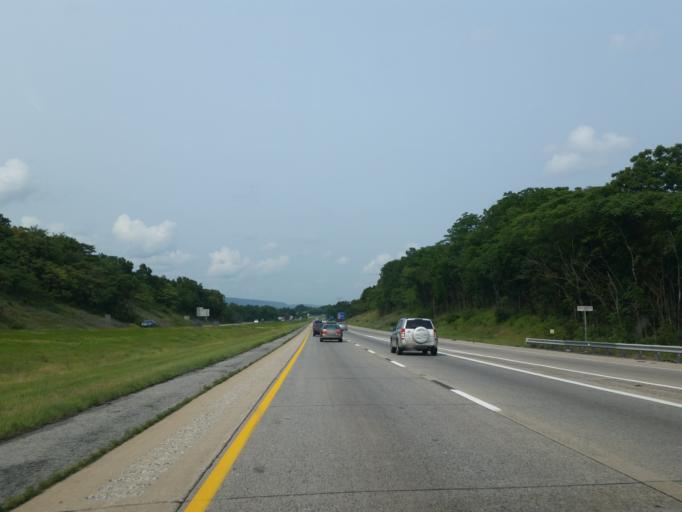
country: US
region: Pennsylvania
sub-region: Dauphin County
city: Skyline View
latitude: 40.3554
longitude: -76.7167
